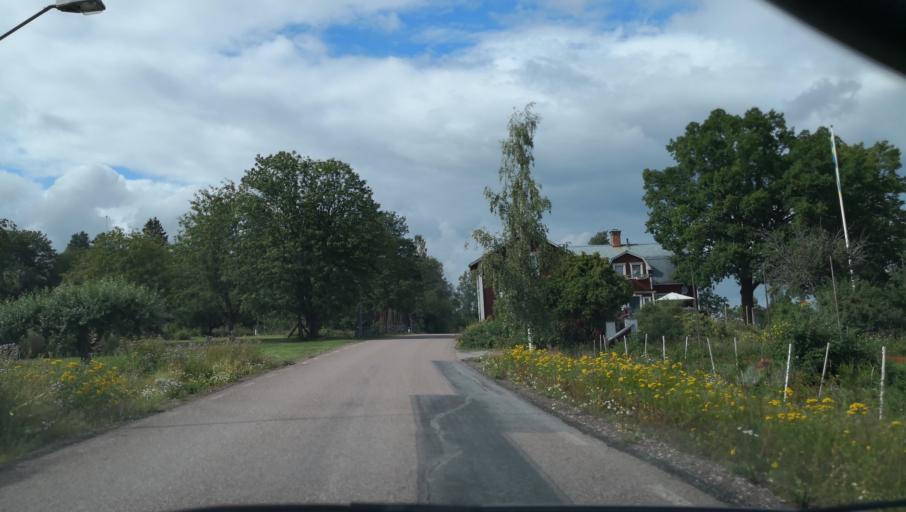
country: SE
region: Dalarna
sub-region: Borlange Kommun
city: Ornas
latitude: 60.4244
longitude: 15.6173
